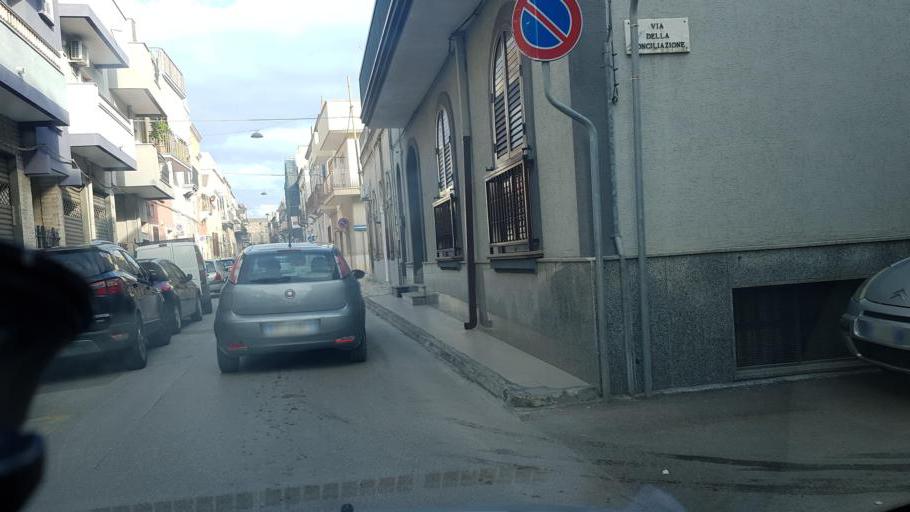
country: IT
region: Apulia
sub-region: Provincia di Brindisi
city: Francavilla Fontana
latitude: 40.5310
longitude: 17.5784
